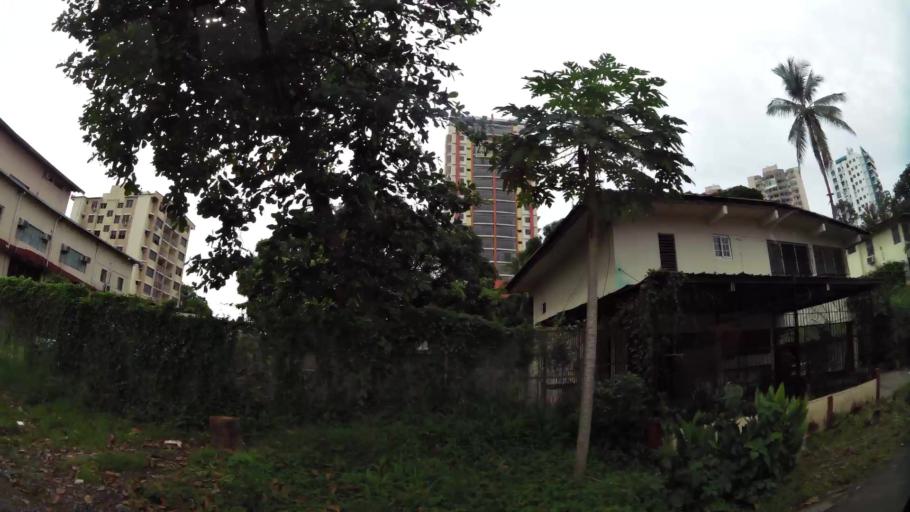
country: PA
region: Panama
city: Panama
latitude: 9.0170
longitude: -79.5183
